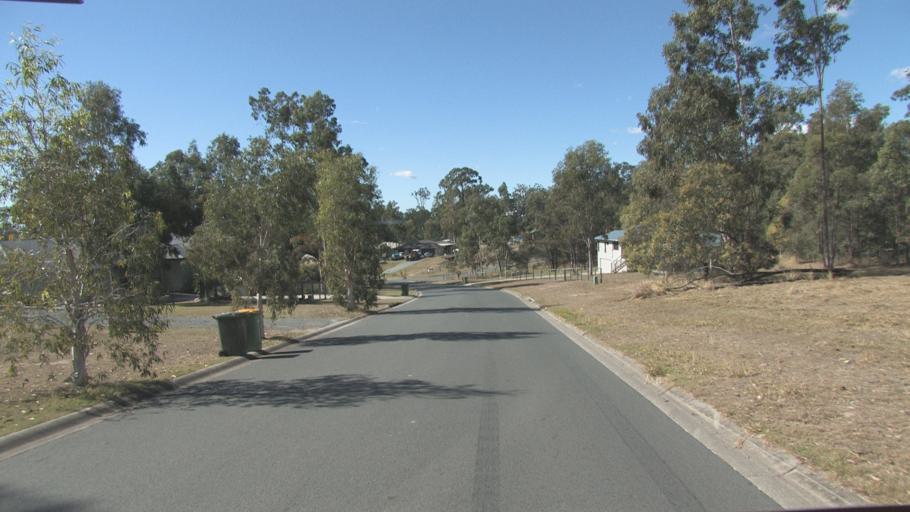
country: AU
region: Queensland
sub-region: Logan
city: North Maclean
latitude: -27.7542
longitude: 152.9389
